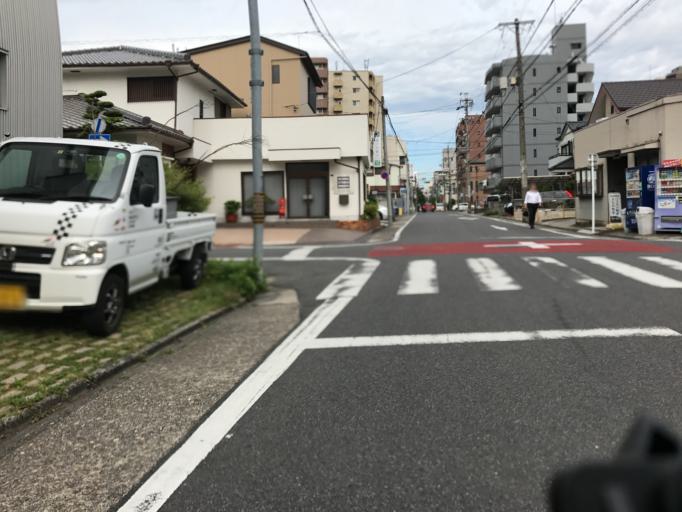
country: JP
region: Aichi
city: Nagoya-shi
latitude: 35.1669
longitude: 136.9427
